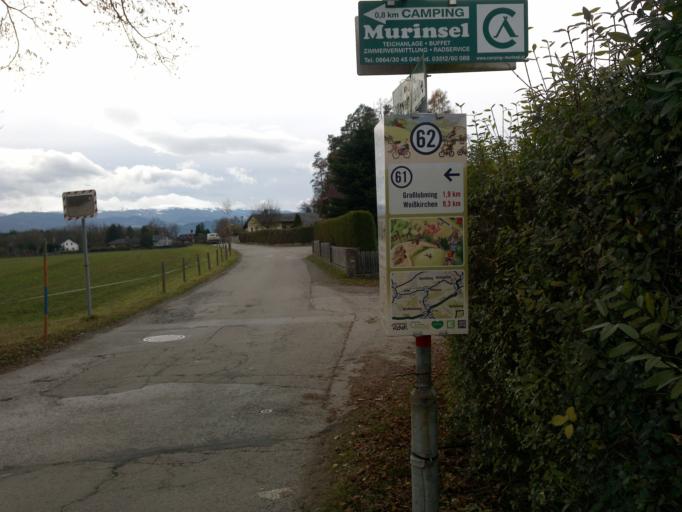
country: AT
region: Styria
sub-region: Politischer Bezirk Murtal
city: Grosslobming
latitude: 47.1987
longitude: 14.8087
